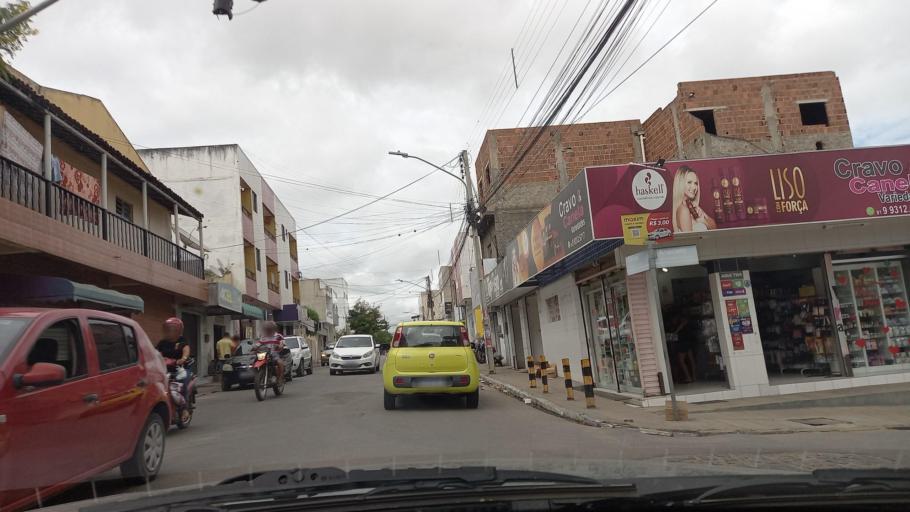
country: BR
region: Pernambuco
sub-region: Caruaru
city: Caruaru
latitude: -8.2735
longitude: -35.9598
